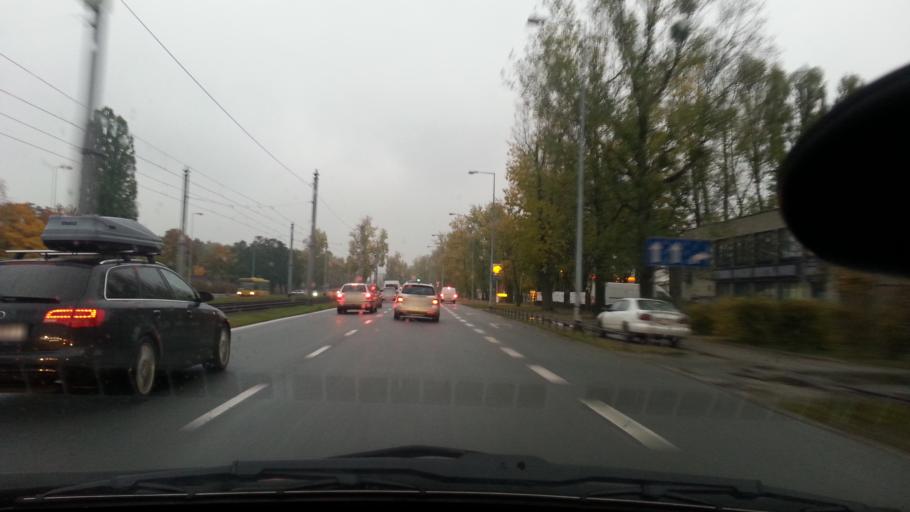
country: PL
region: Masovian Voivodeship
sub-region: Warszawa
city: Praga Polnoc
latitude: 52.2758
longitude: 21.0295
